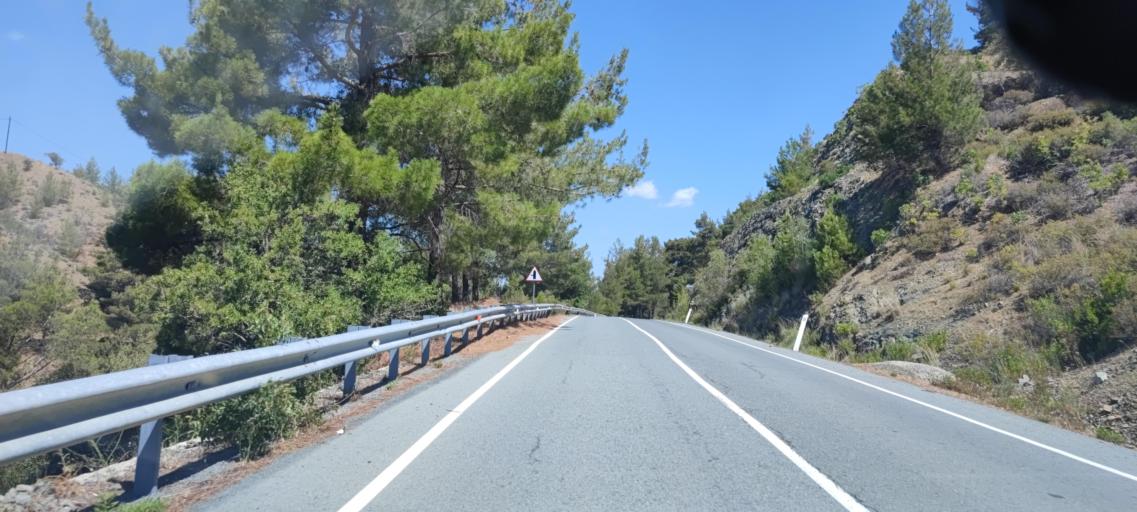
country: CY
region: Lefkosia
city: Kakopetria
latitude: 34.9158
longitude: 32.8145
